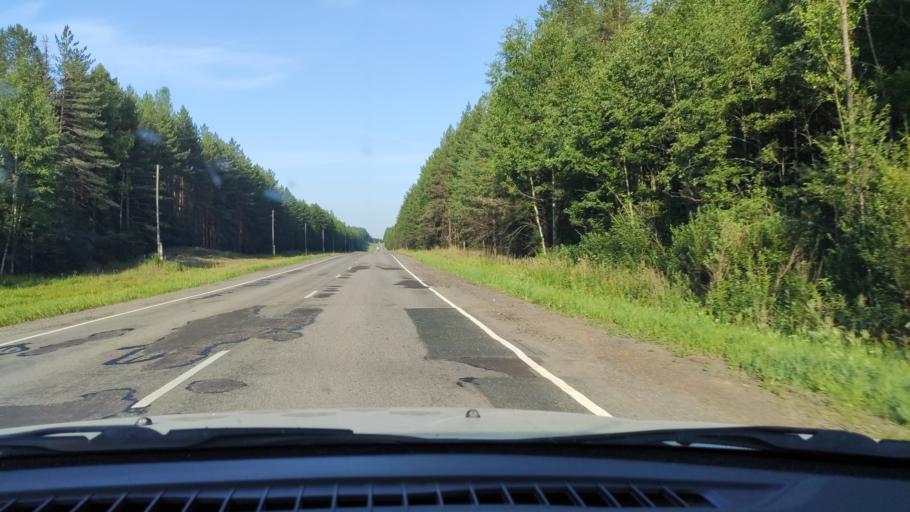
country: RU
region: Kirov
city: Belaya Kholunitsa
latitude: 58.9081
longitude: 50.9805
